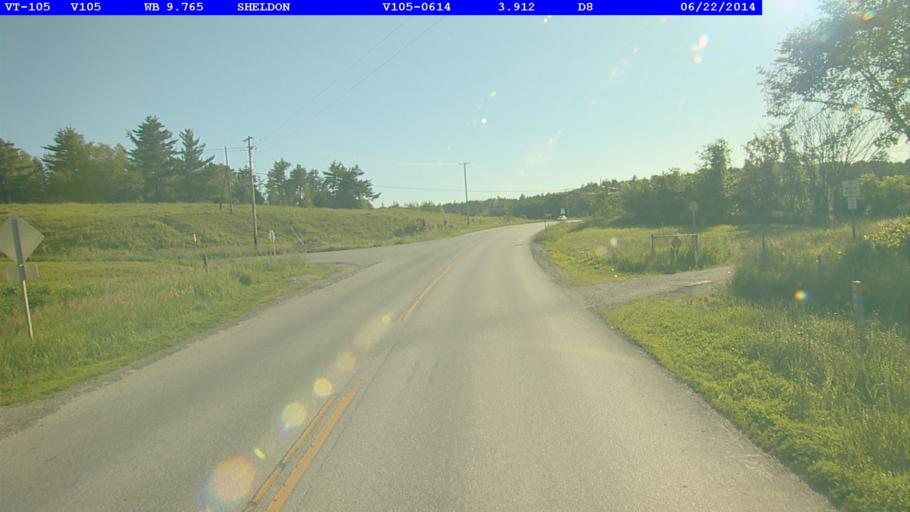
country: US
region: Vermont
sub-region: Franklin County
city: Enosburg Falls
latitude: 44.9002
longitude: -72.9549
